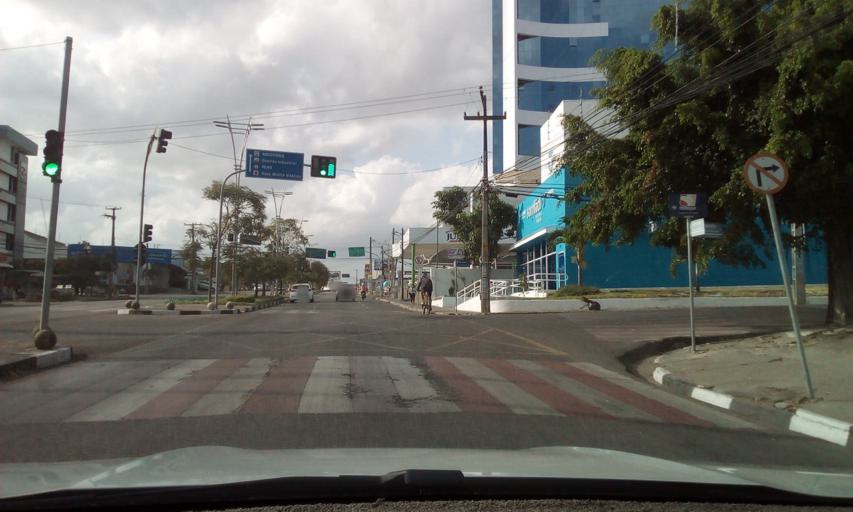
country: BR
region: Pernambuco
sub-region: Caruaru
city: Caruaru
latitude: -8.2708
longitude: -35.9754
